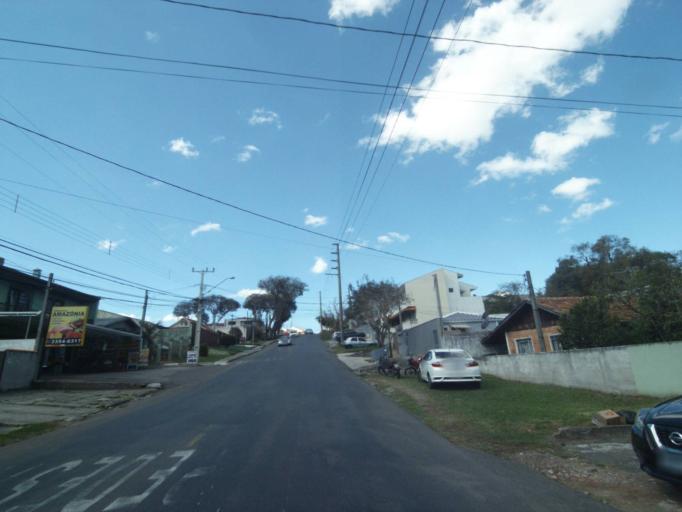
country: BR
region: Parana
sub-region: Curitiba
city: Curitiba
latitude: -25.3785
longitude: -49.2543
